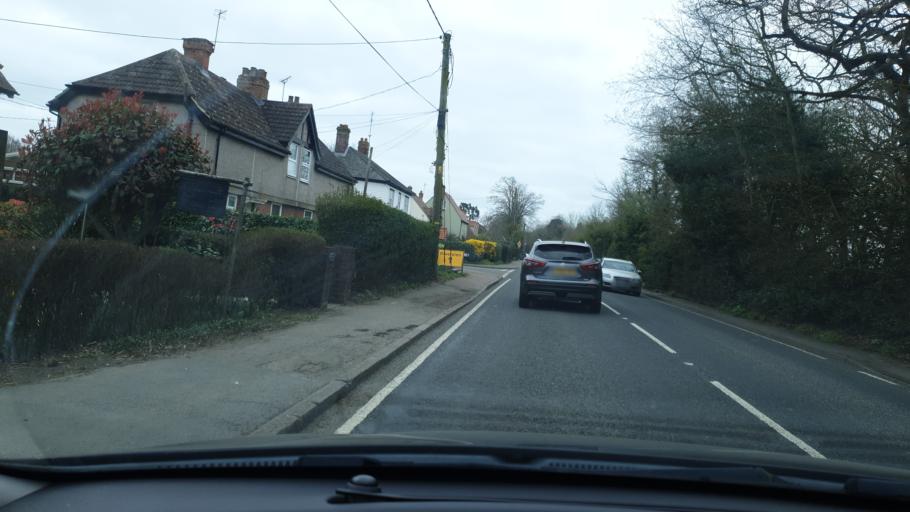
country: GB
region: England
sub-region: Essex
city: Great Horkesley
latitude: 51.9351
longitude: 0.8760
